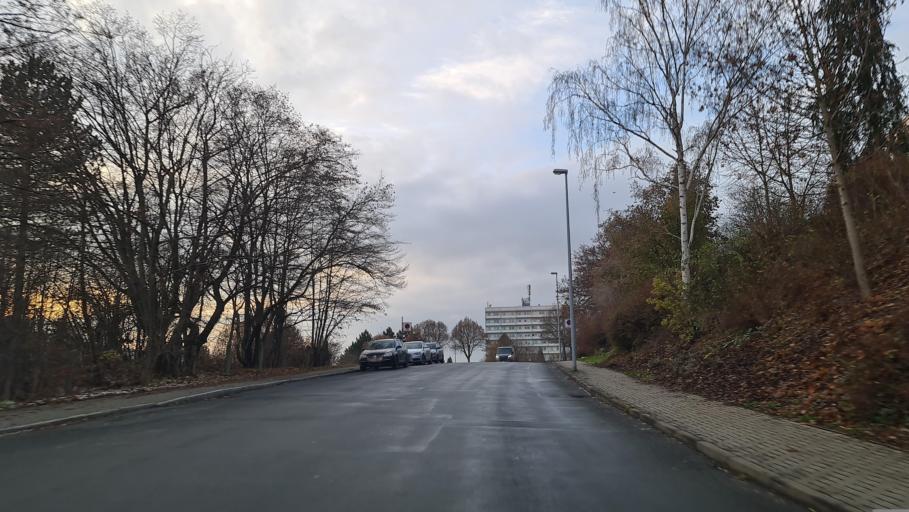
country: DE
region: Saxony
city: Reichenbach/Vogtland
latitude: 50.6234
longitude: 12.2880
